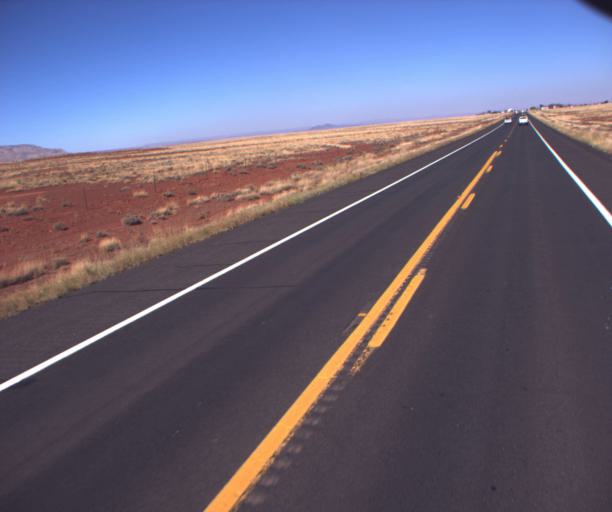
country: US
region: Arizona
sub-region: Coconino County
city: Tuba City
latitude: 35.7319
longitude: -111.4798
